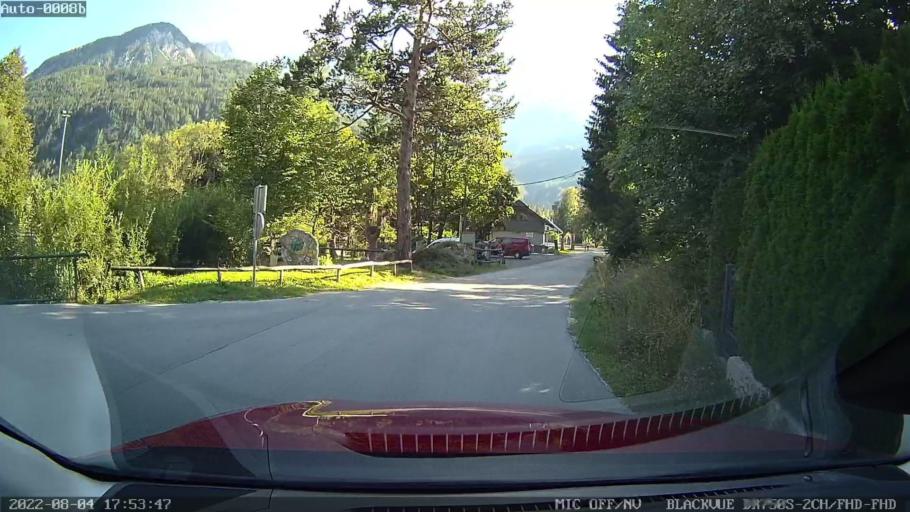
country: SI
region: Kranjska Gora
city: Mojstrana
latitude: 46.4855
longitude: 13.8429
